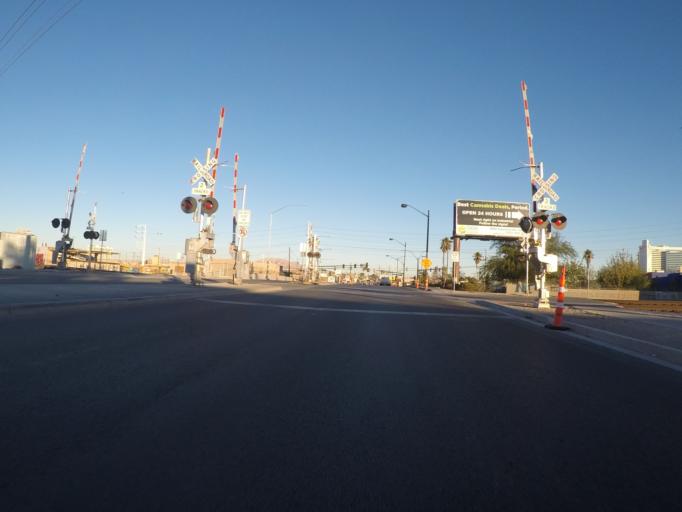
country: US
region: Nevada
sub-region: Clark County
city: Las Vegas
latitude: 36.1525
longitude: -115.1609
